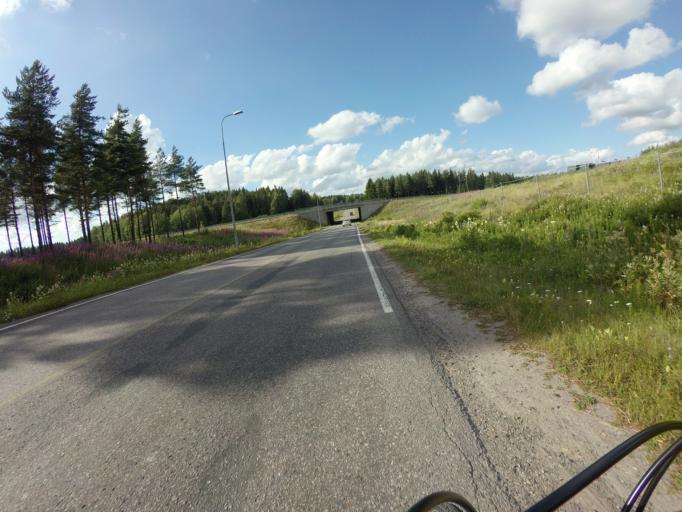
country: FI
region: Varsinais-Suomi
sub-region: Turku
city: Vahto
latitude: 60.5428
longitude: 22.3409
